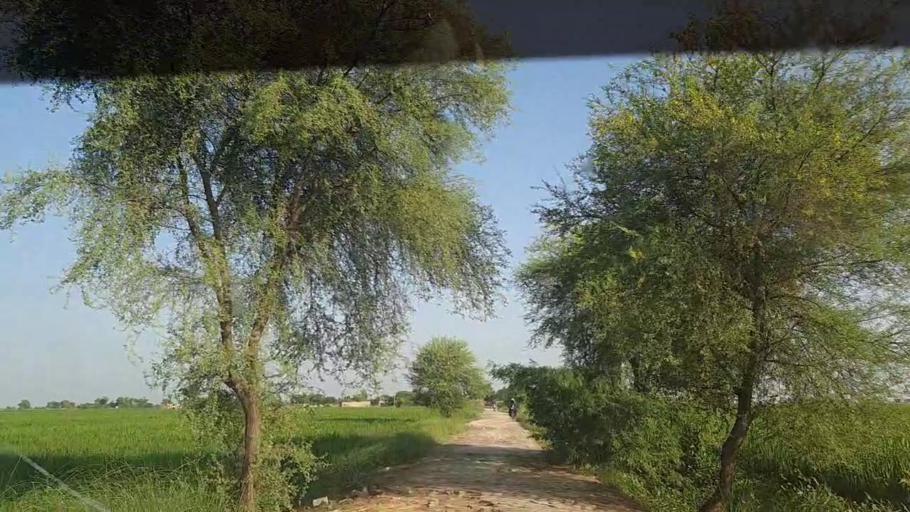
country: PK
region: Sindh
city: Tangwani
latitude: 28.2696
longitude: 69.0103
